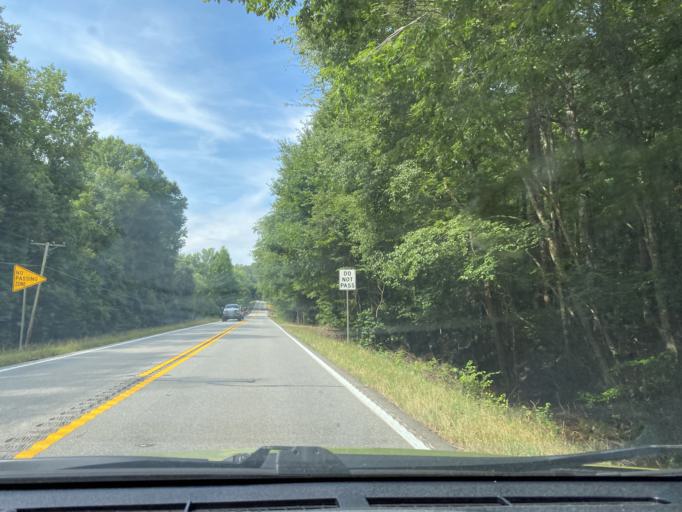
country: US
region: Georgia
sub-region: Coweta County
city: East Newnan
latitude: 33.2789
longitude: -84.7018
